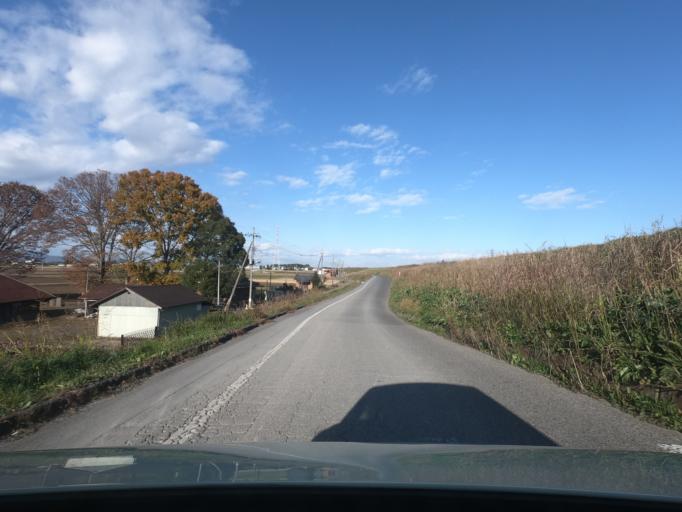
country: JP
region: Ibaraki
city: Koga
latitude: 36.2489
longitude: 139.7339
